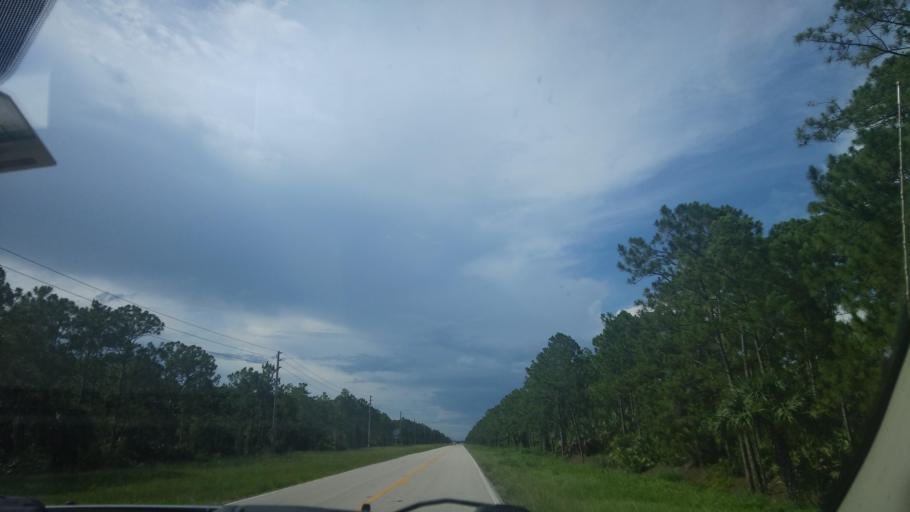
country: US
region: Florida
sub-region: Brevard County
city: Grant-Valkaria
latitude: 27.8748
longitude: -80.6227
